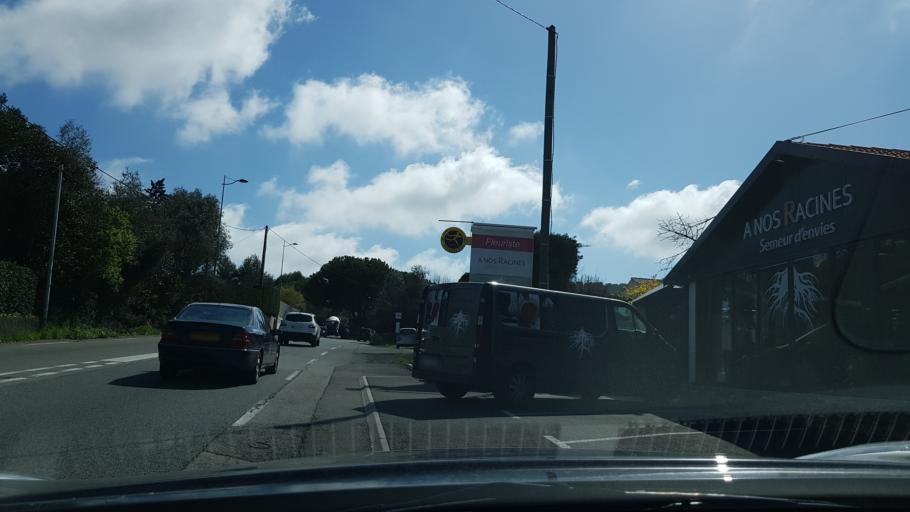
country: FR
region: Provence-Alpes-Cote d'Azur
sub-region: Departement des Alpes-Maritimes
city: Vallauris
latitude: 43.5906
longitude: 7.0562
